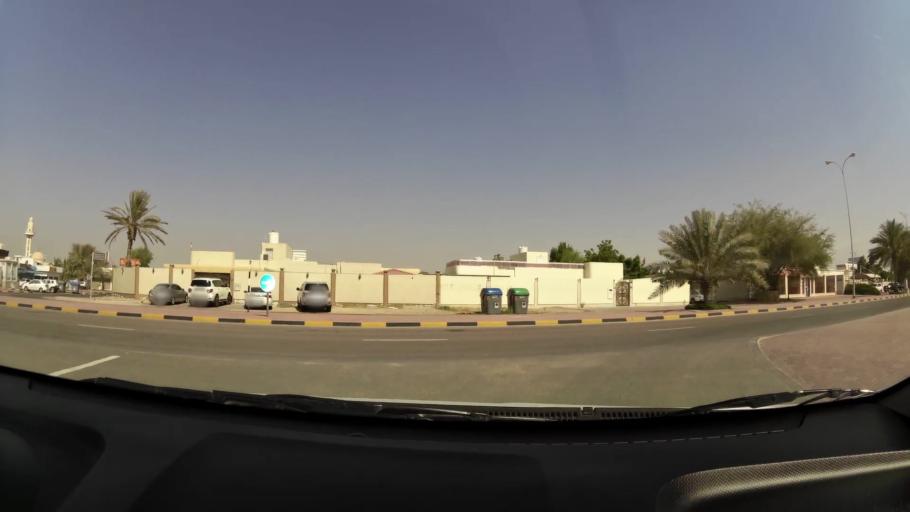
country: AE
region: Ajman
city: Ajman
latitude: 25.4098
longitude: 55.4744
